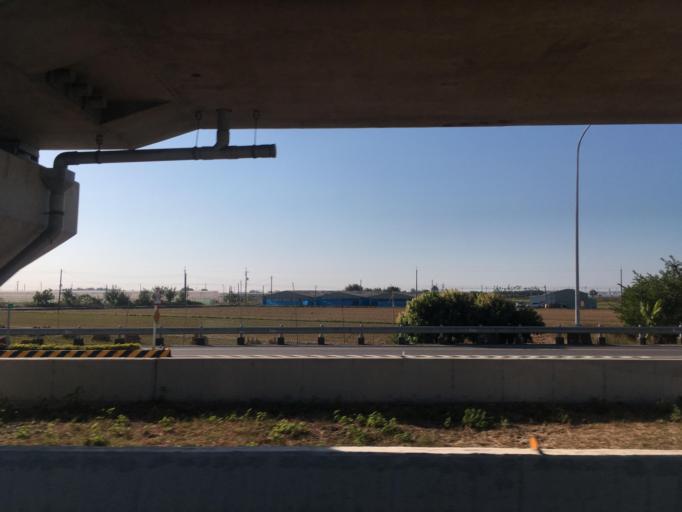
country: TW
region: Taiwan
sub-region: Chiayi
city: Taibao
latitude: 23.4413
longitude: 120.3231
